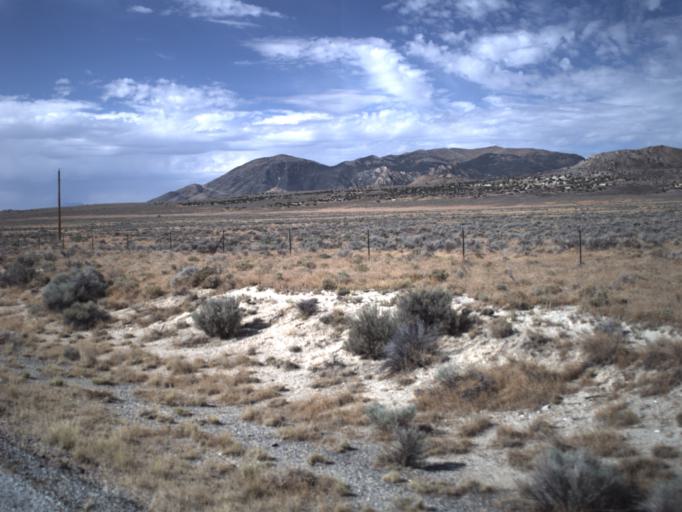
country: US
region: Utah
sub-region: Tooele County
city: Wendover
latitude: 41.5357
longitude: -113.5921
